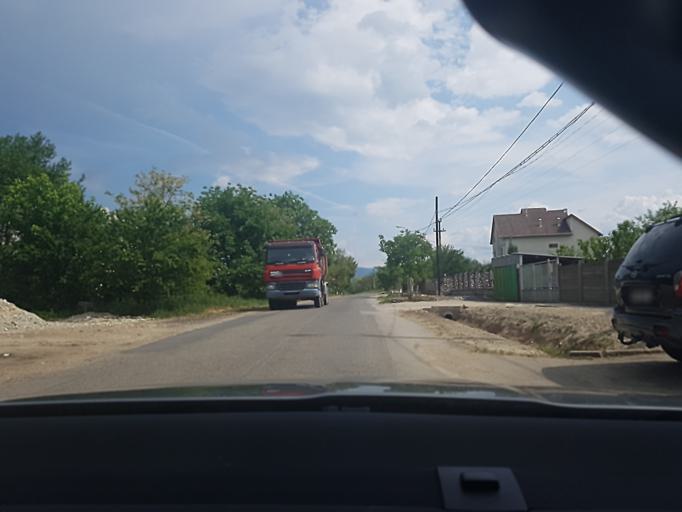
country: RO
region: Hunedoara
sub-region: Comuna Calan
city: Calan
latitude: 45.7224
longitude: 23.0238
